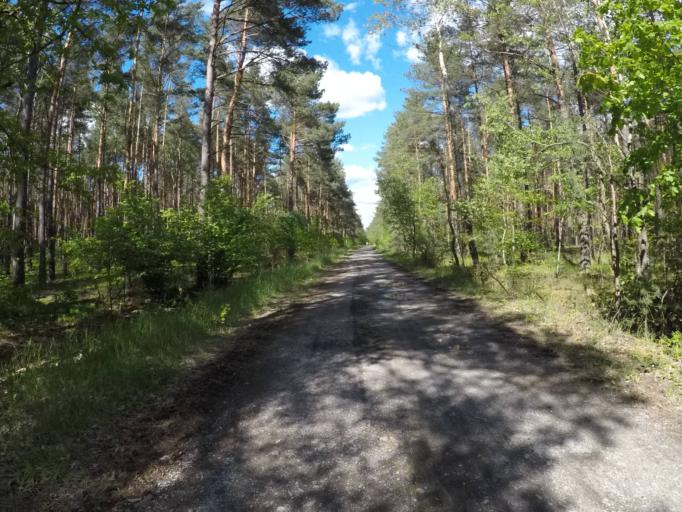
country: PL
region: Swietokrzyskie
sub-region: Powiat kielecki
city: Kostomloty Drugie
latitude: 50.8926
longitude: 20.5423
